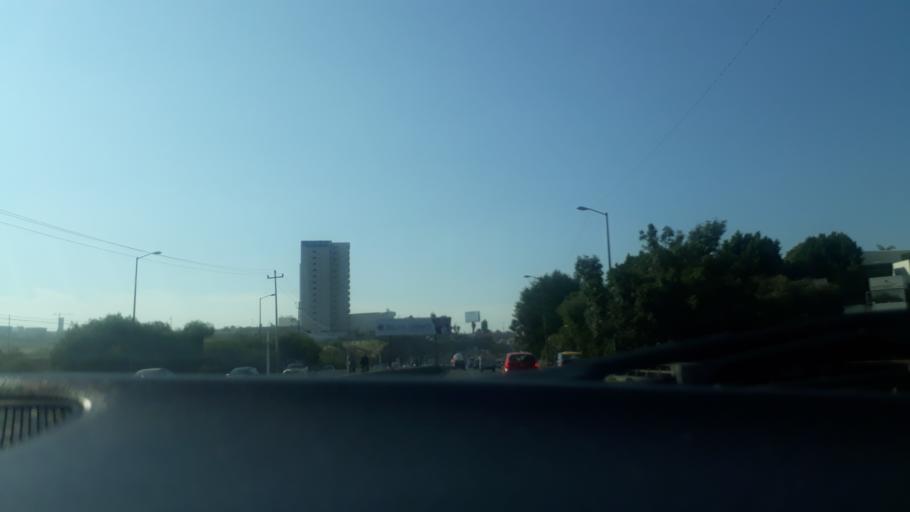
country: MX
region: Puebla
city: Tlazcalancingo
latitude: 18.9973
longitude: -98.2571
